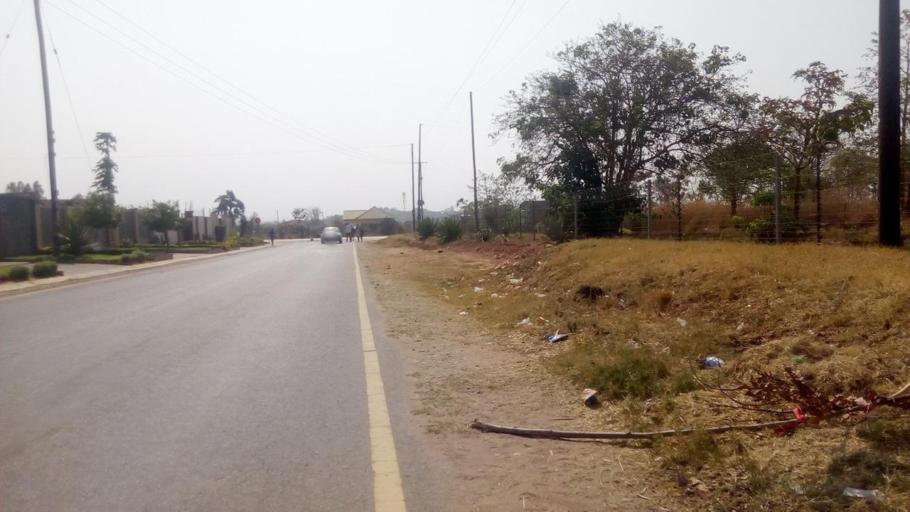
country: ZM
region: Lusaka
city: Lusaka
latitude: -15.3625
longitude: 28.2822
